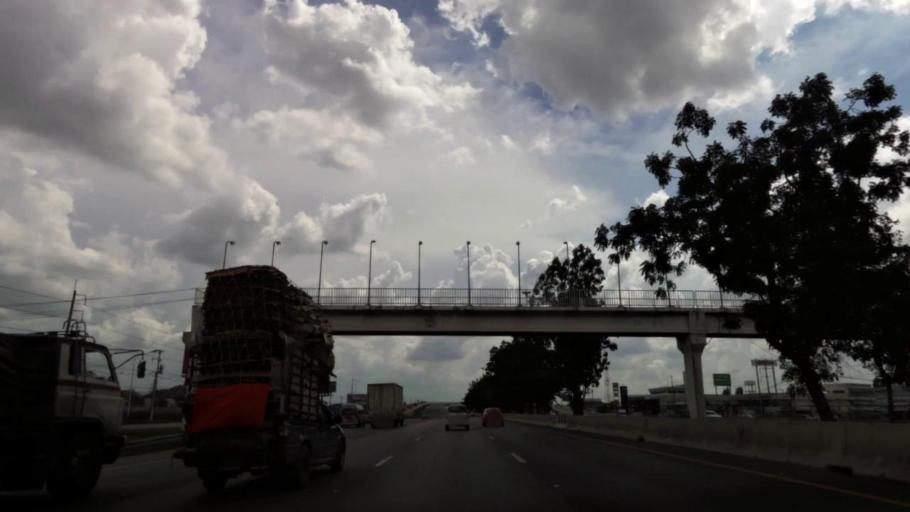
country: TH
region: Phra Nakhon Si Ayutthaya
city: Phra Nakhon Si Ayutthaya
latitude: 14.3163
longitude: 100.6134
